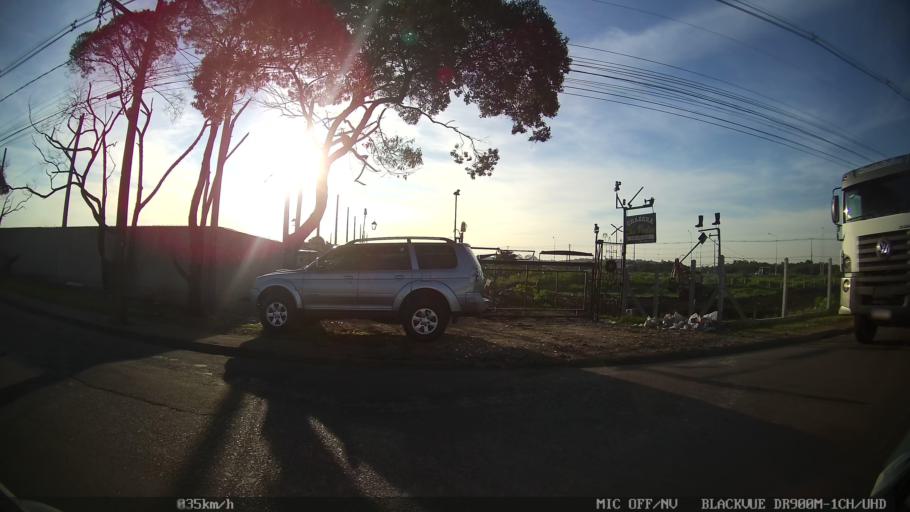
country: BR
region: Parana
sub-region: Pinhais
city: Pinhais
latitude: -25.4467
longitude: -49.1404
